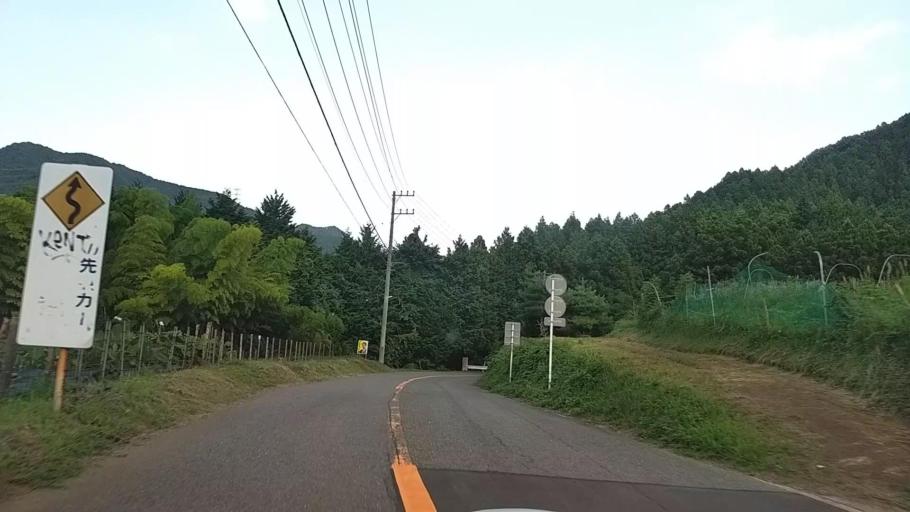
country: JP
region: Yamanashi
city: Uenohara
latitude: 35.6128
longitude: 139.2090
